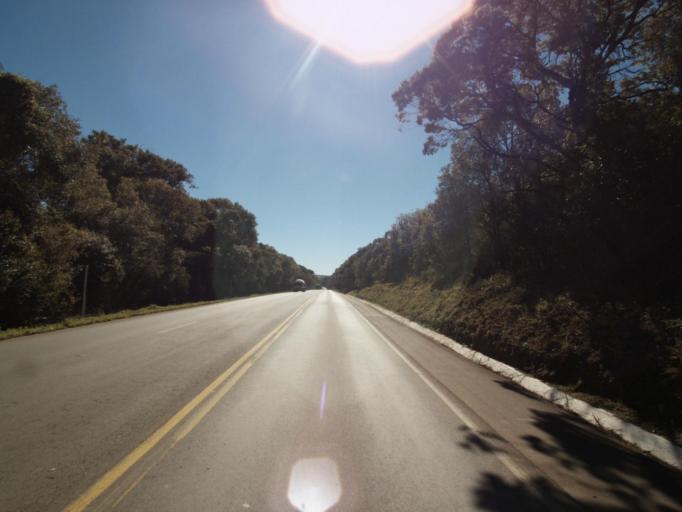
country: BR
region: Santa Catarina
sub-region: Concordia
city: Concordia
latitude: -26.9621
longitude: -51.8549
